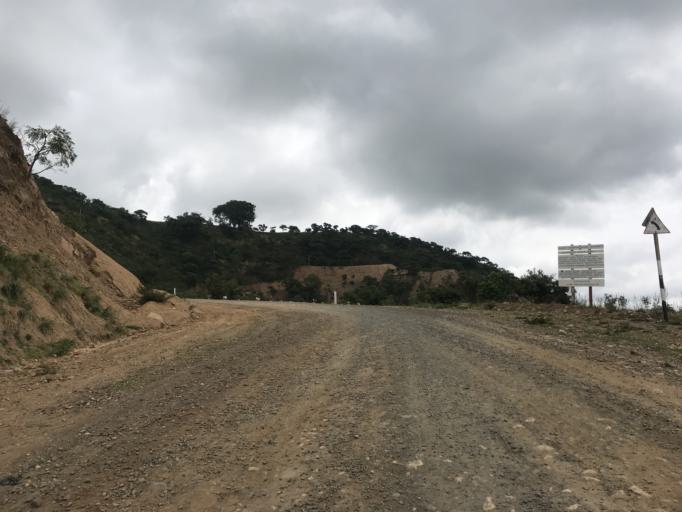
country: ET
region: Oromiya
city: Shambu
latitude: 9.7113
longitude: 36.6303
